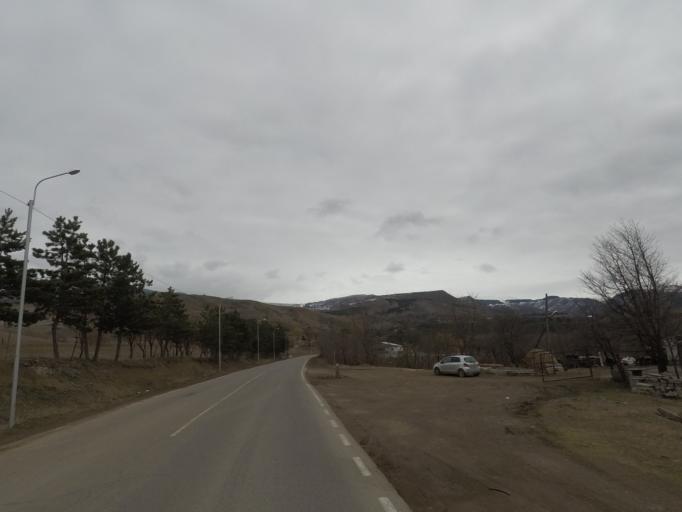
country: GE
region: Samtskhe-Javakheti
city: Aspindza
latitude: 41.5881
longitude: 43.2352
